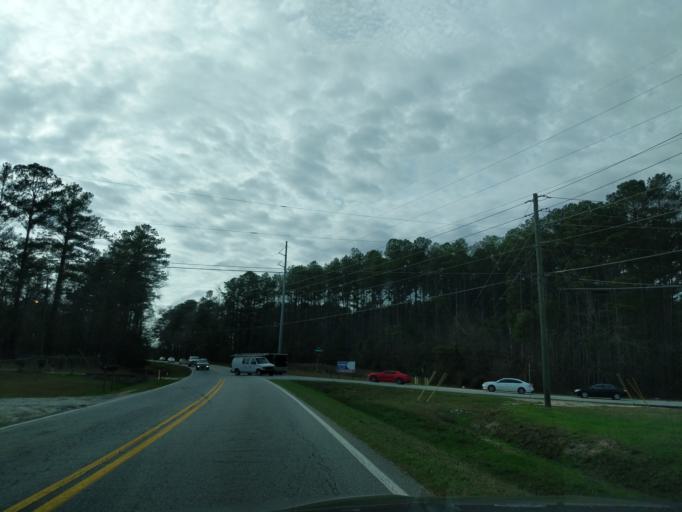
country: US
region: Georgia
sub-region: Columbia County
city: Evans
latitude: 33.4762
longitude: -82.1394
